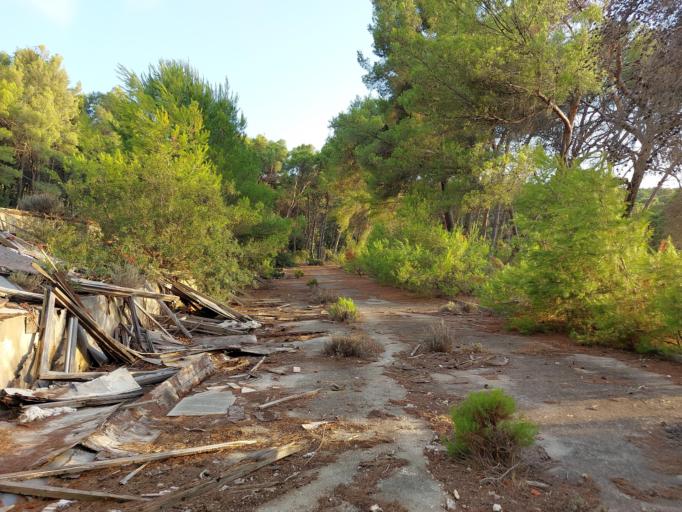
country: HR
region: Dubrovacko-Neretvanska
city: Smokvica
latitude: 42.7376
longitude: 16.8289
